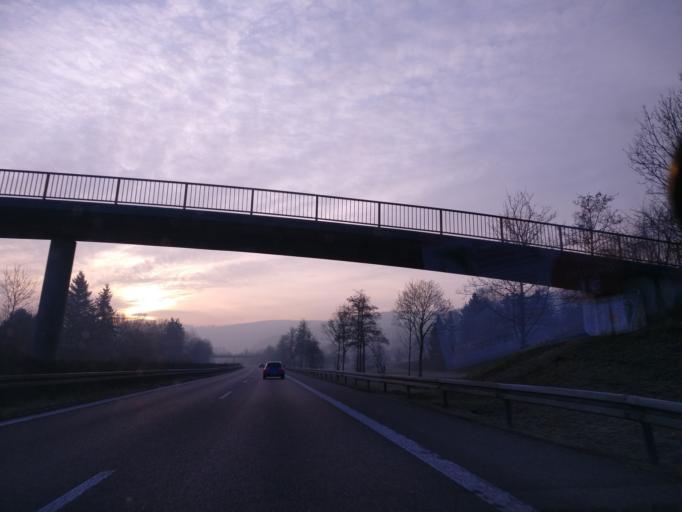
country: DE
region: Baden-Wuerttemberg
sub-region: Regierungsbezirk Stuttgart
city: Pluderhausen
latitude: 48.7869
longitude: 9.5997
